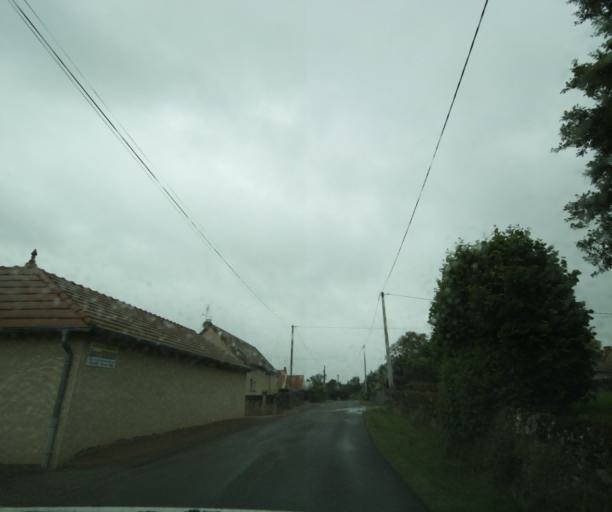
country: FR
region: Bourgogne
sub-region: Departement de Saone-et-Loire
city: Palinges
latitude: 46.4931
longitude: 4.1996
